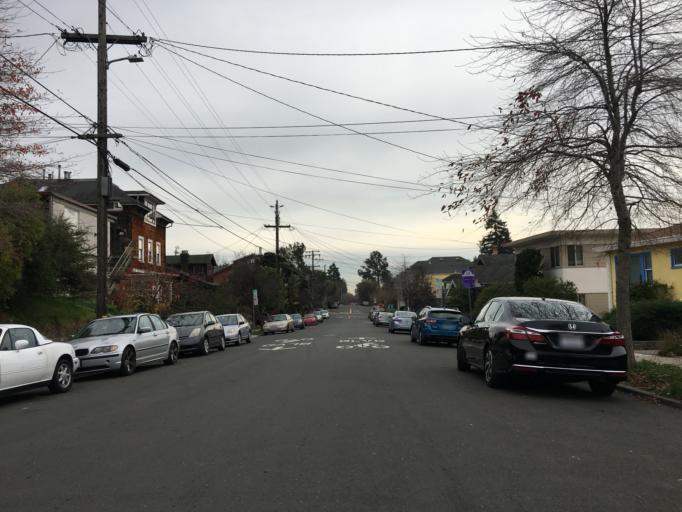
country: US
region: California
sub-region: Alameda County
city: Berkeley
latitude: 37.8829
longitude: -122.2720
